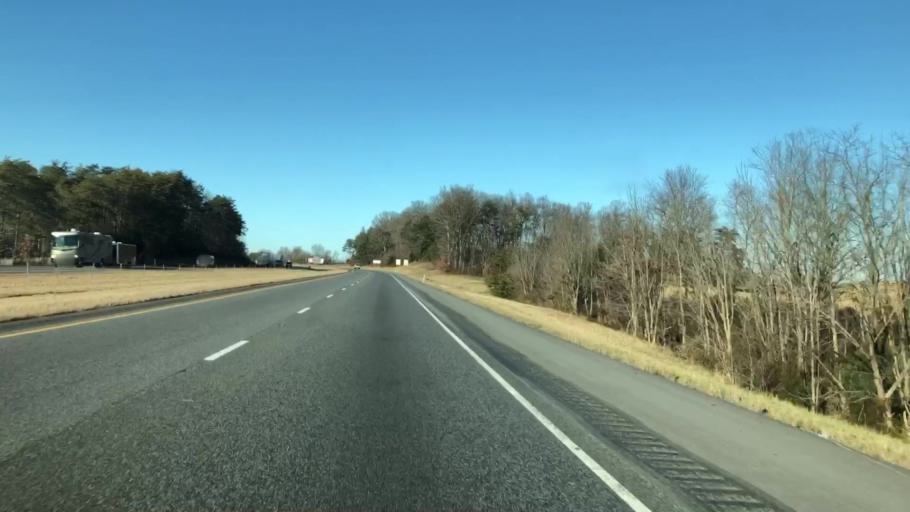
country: US
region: Indiana
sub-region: Clark County
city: Henryville
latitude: 38.5922
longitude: -85.7782
